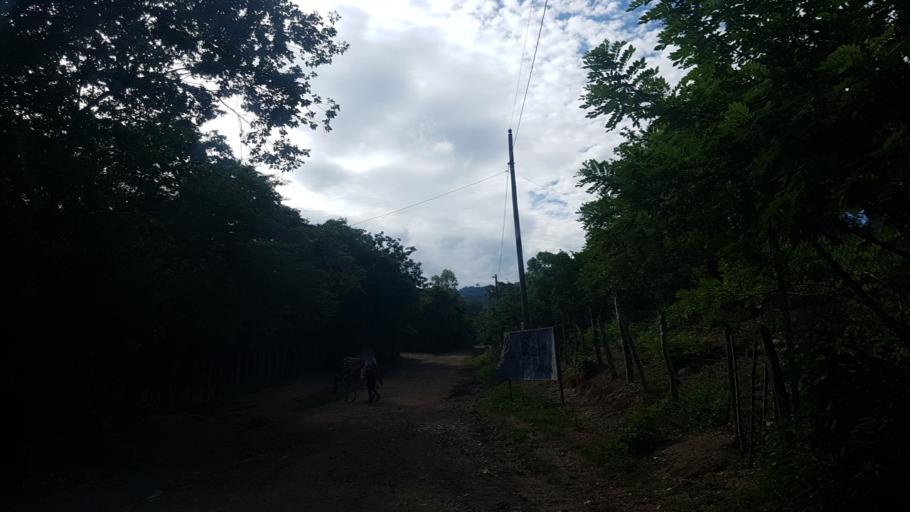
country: NI
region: Nueva Segovia
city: Ocotal
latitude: 13.6122
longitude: -86.4488
